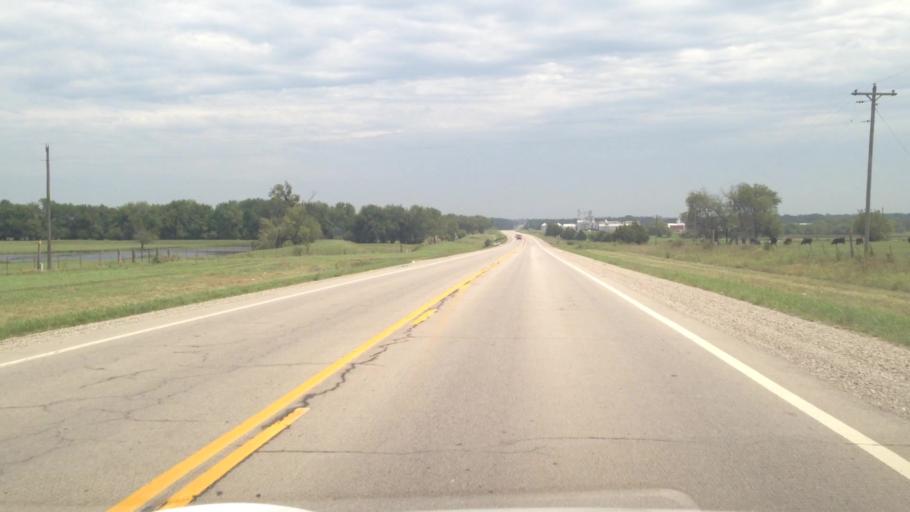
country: US
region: Kansas
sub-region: Crawford County
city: Girard
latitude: 37.5144
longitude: -94.9235
